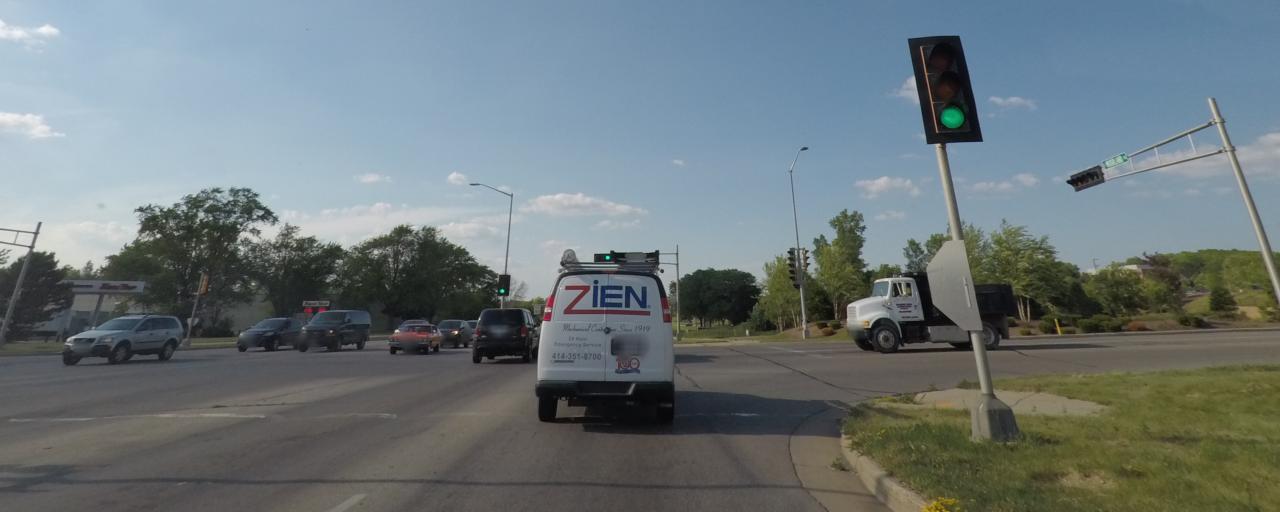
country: US
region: Wisconsin
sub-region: Waukesha County
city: New Berlin
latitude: 42.9443
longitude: -88.1089
